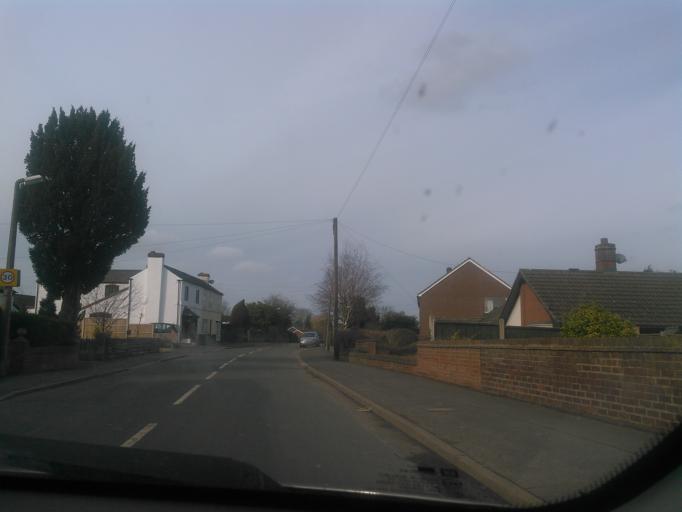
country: GB
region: England
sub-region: Shropshire
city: Bicton
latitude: 52.7715
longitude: -2.7805
